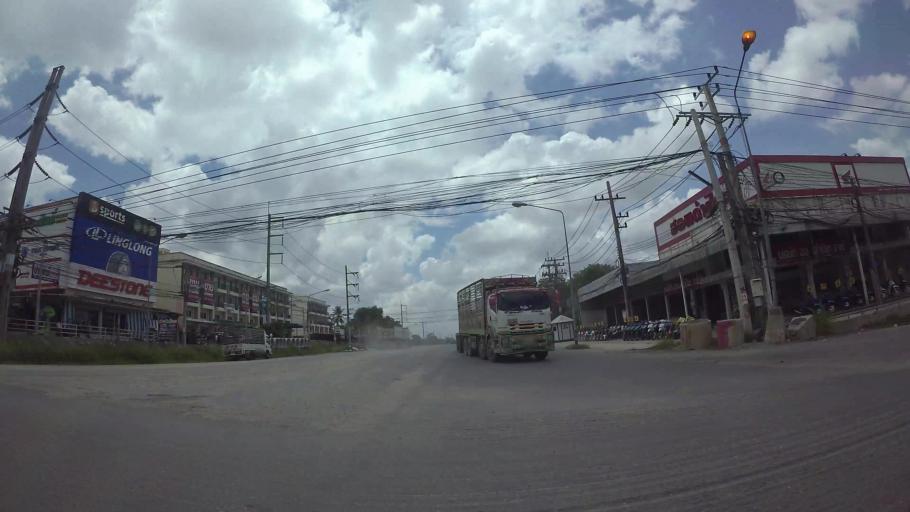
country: TH
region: Rayong
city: Nikhom Phattana
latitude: 12.8612
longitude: 101.0838
